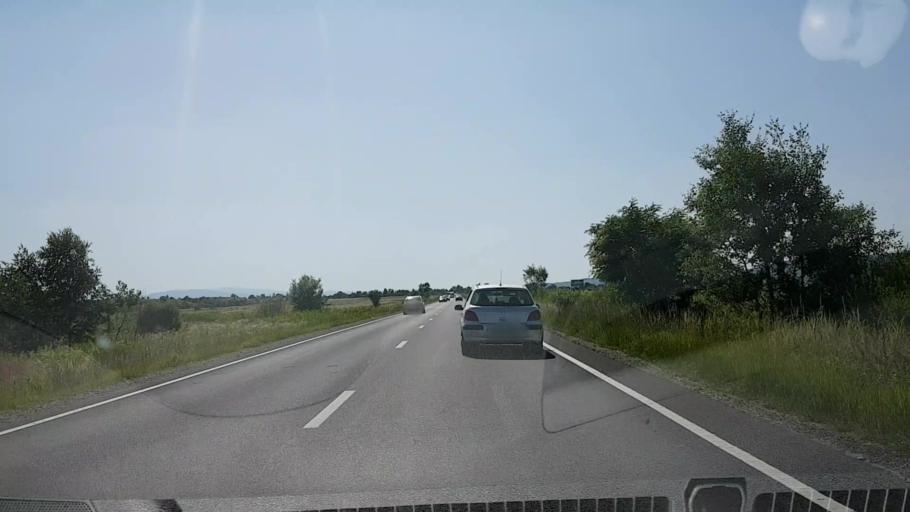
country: RO
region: Sibiu
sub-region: Comuna Porumbacu de Jos
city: Porumbacu de Jos
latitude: 45.7568
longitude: 24.4765
